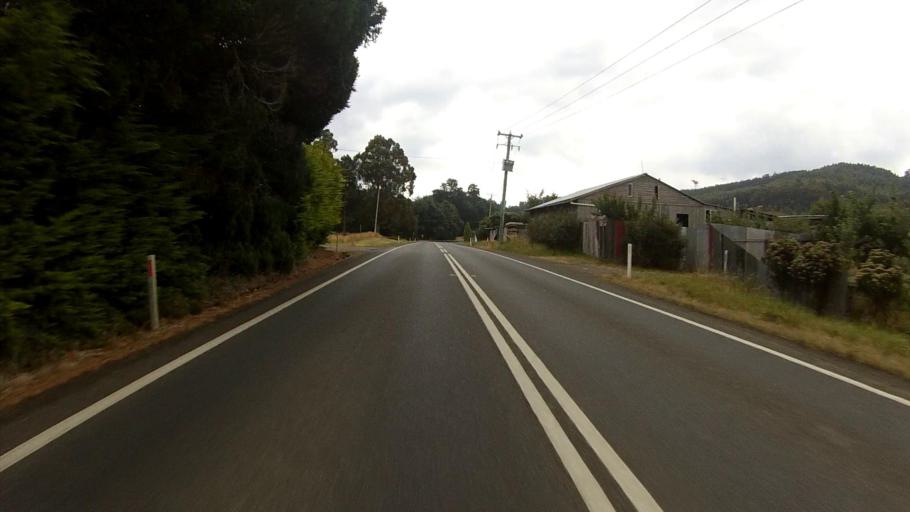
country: AU
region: Tasmania
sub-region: Huon Valley
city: Cygnet
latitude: -43.1378
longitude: 147.0564
